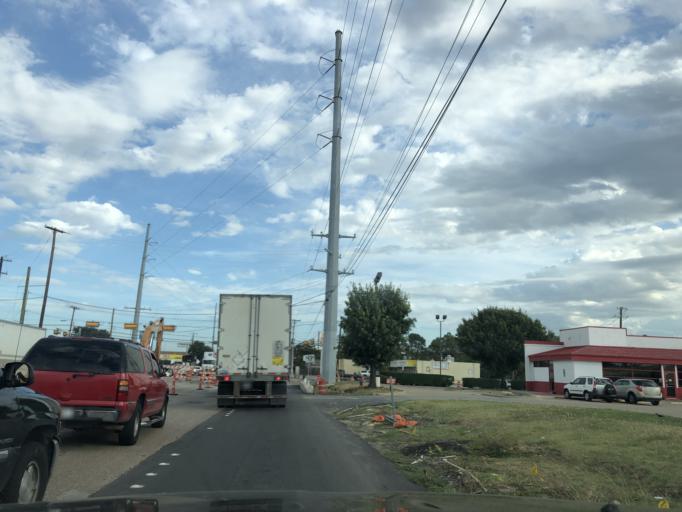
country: US
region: Texas
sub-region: Dallas County
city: Garland
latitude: 32.8780
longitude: -96.6654
